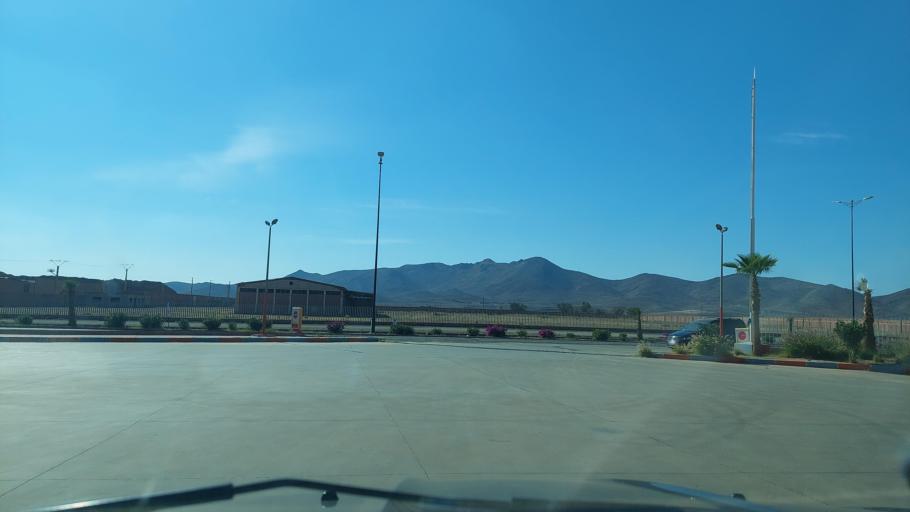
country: MA
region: Marrakech-Tensift-Al Haouz
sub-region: Marrakech
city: Marrakesh
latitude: 31.7521
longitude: -7.9777
